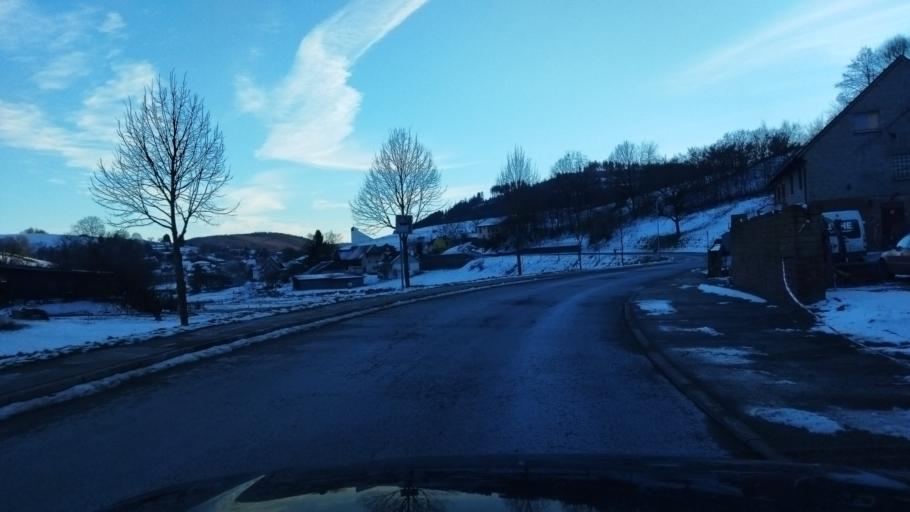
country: DE
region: Hesse
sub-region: Regierungsbezirk Darmstadt
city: Beerfelden
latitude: 49.5385
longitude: 9.0107
